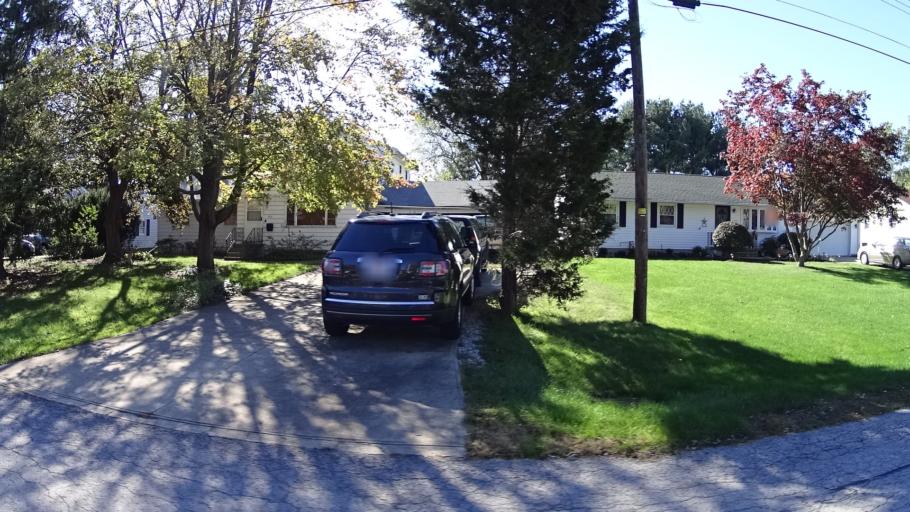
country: US
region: Ohio
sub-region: Lorain County
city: Amherst
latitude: 41.3964
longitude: -82.2422
